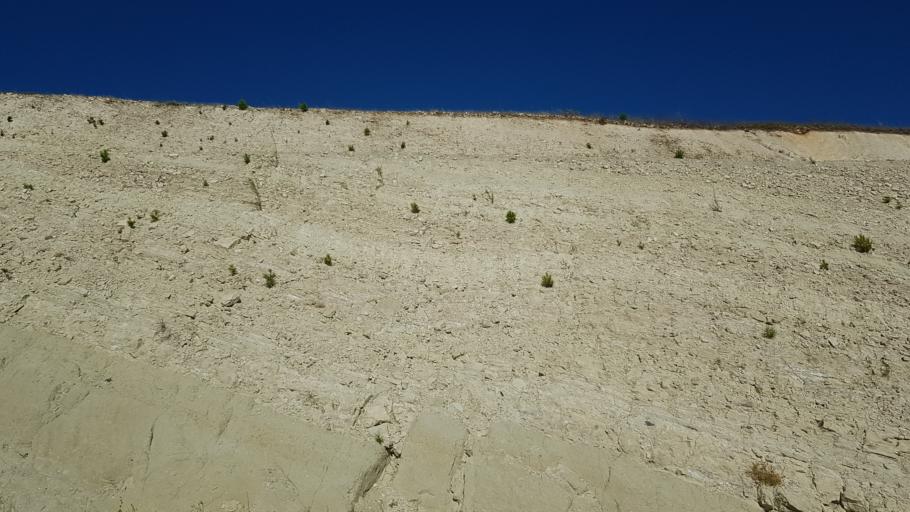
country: TR
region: Balikesir
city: Ertugrul
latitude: 39.5632
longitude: 27.7022
